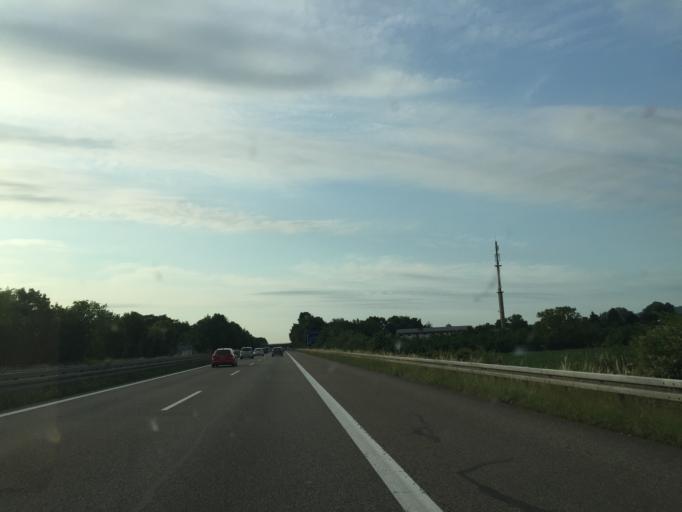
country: DE
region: Baden-Wuerttemberg
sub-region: Karlsruhe Region
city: Schriesheim
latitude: 49.4702
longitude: 8.6429
